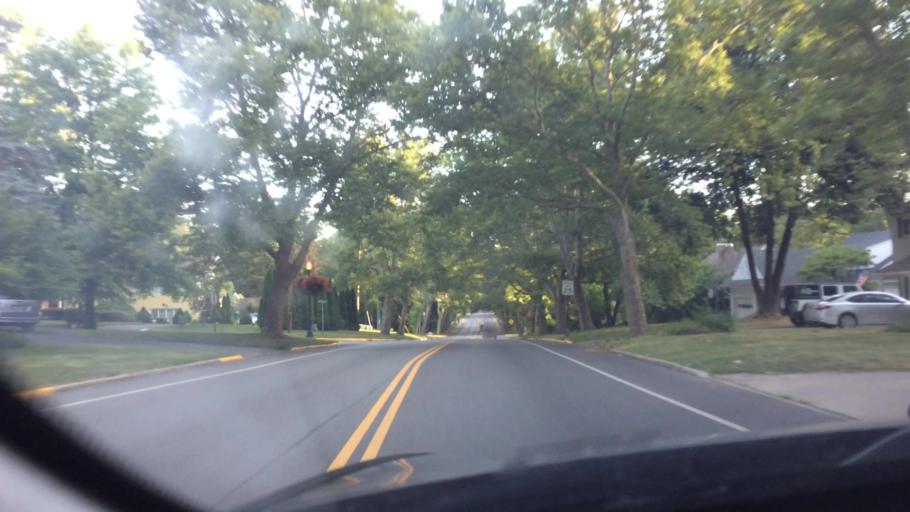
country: US
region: Ohio
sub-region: Lucas County
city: Ottawa Hills
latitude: 41.6630
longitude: -83.6435
